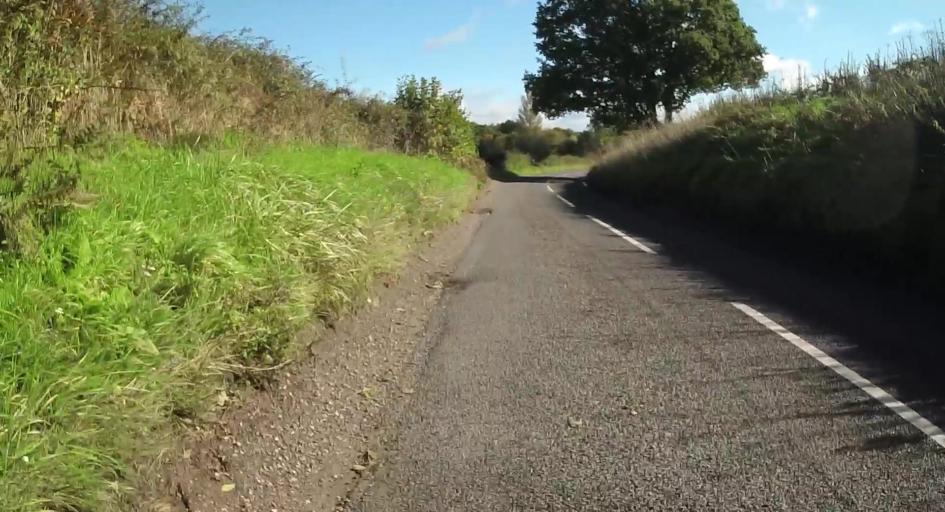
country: GB
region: England
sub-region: Hampshire
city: Old Basing
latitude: 51.2649
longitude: -1.0105
